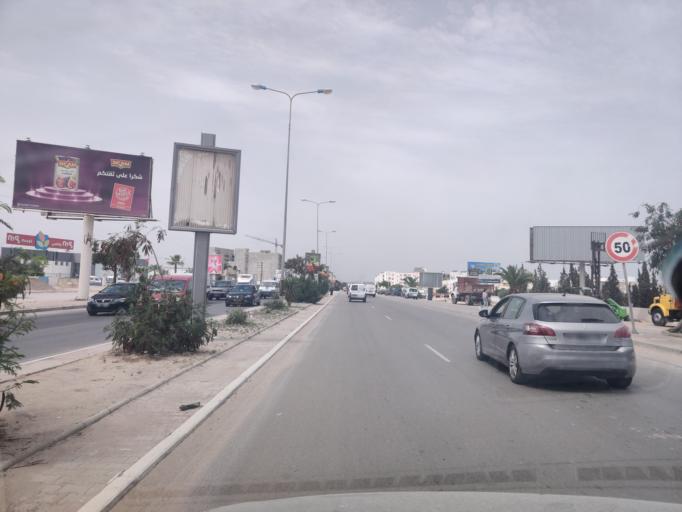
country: TN
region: Susah
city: Hammam Sousse
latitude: 35.8347
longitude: 10.5887
